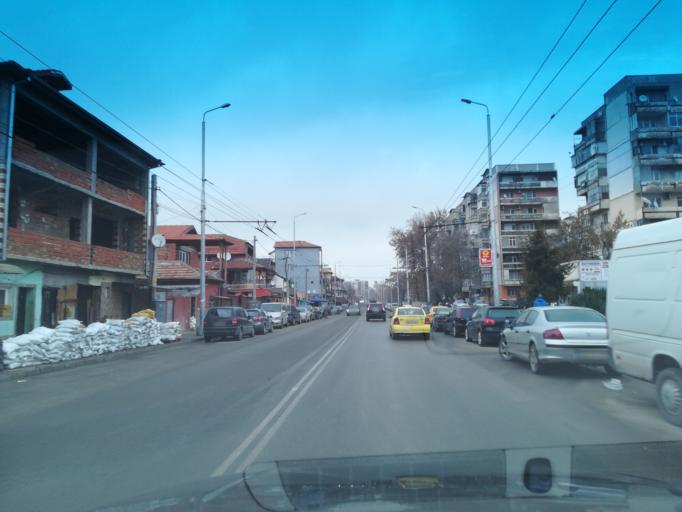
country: BG
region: Plovdiv
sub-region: Obshtina Plovdiv
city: Plovdiv
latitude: 42.1511
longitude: 24.7868
